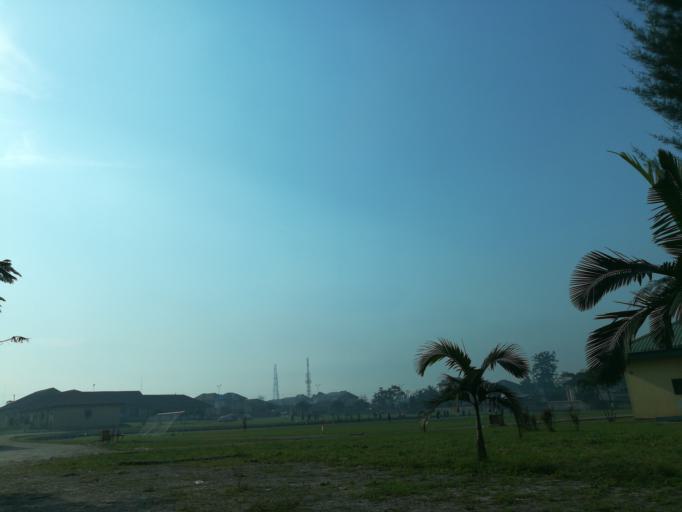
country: NG
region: Rivers
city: Port Harcourt
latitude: 4.8151
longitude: 7.0204
